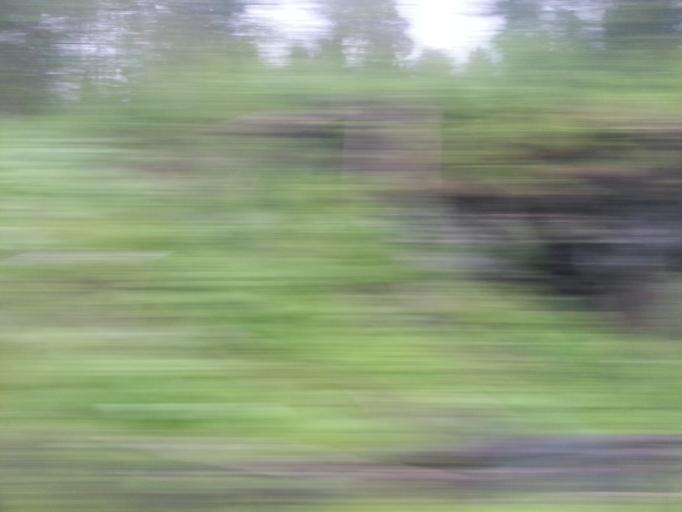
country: NO
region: Sor-Trondelag
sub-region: Rennebu
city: Berkak
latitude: 62.8702
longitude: 10.0866
